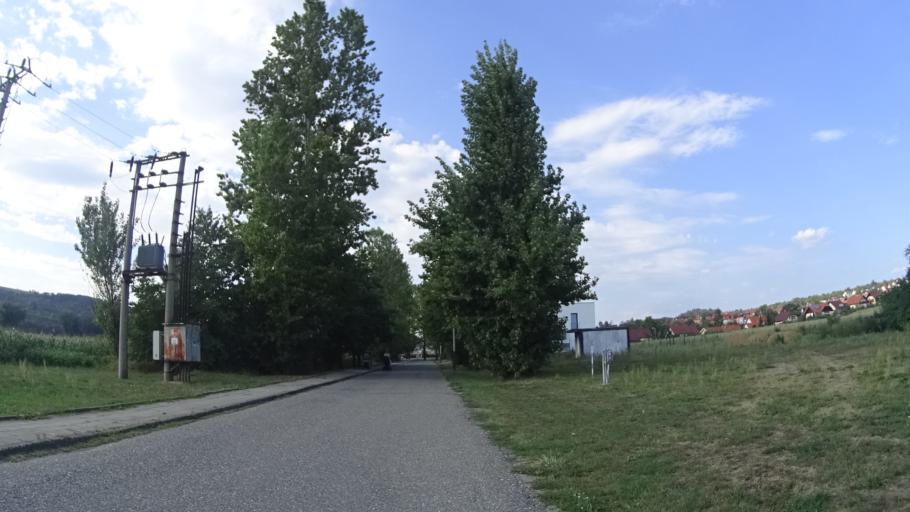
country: CZ
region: Zlin
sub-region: Okres Zlin
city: Napajedla
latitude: 49.1586
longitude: 17.5123
